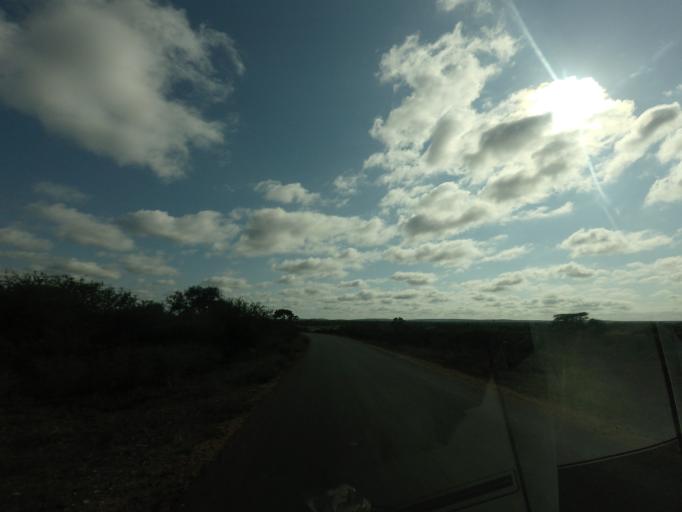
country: ZA
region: Mpumalanga
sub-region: Ehlanzeni District
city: Komatipoort
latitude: -25.1533
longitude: 31.9381
